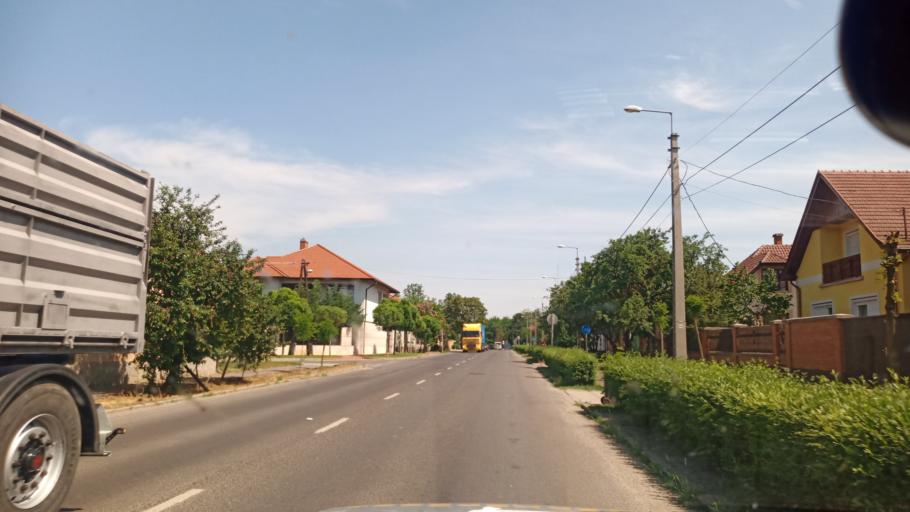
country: HU
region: Bekes
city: Oroshaza
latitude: 46.5580
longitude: 20.6547
